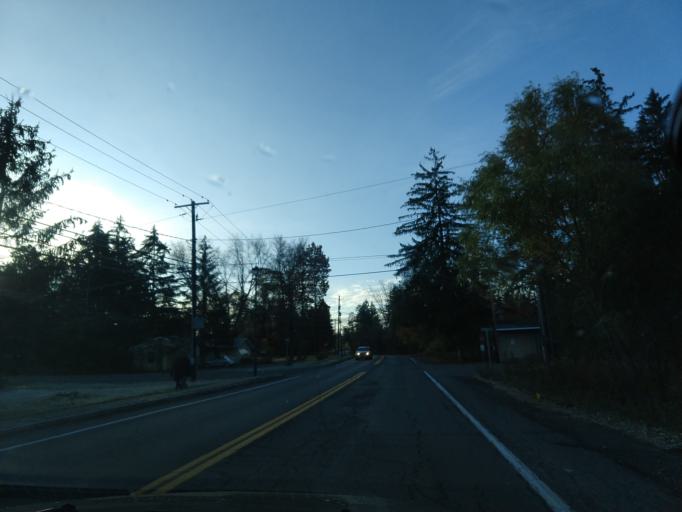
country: US
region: New York
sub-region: Tompkins County
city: Lansing
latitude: 42.4728
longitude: -76.4815
